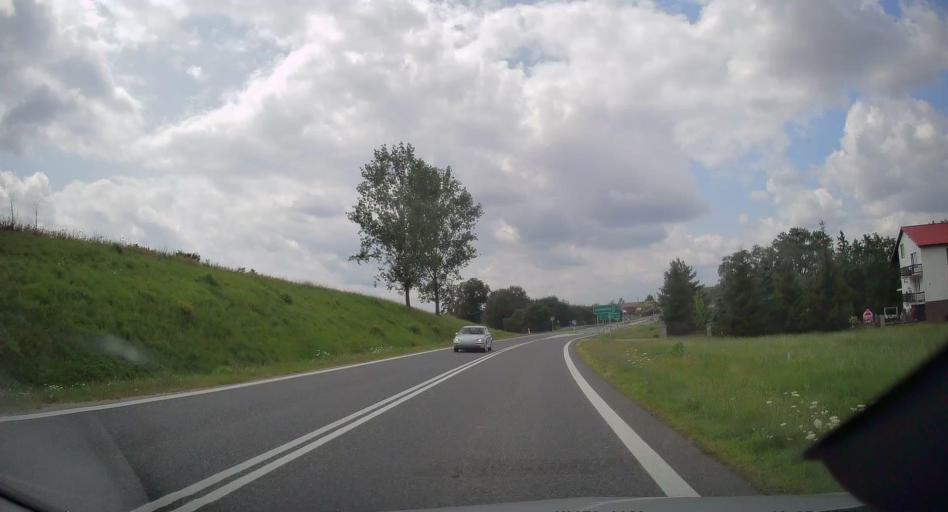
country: CZ
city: Osoblaha
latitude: 50.3335
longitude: 17.7079
